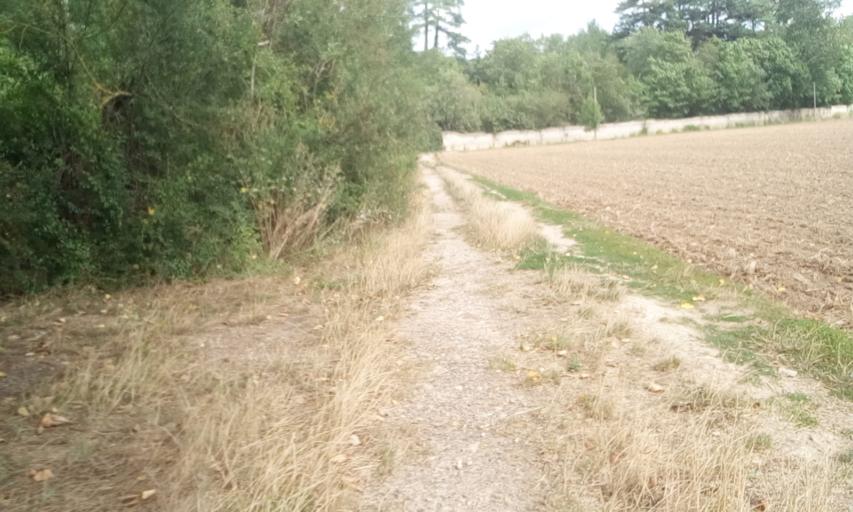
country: FR
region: Lower Normandy
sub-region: Departement du Calvados
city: Bellengreville
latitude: 49.1140
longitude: -0.2362
